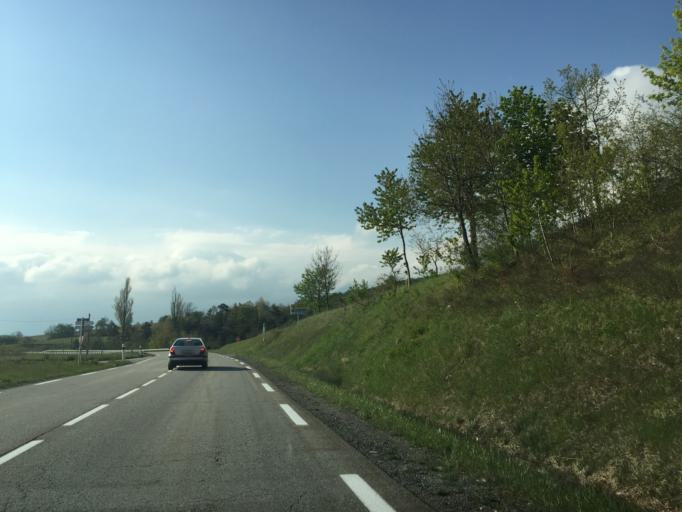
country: FR
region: Rhone-Alpes
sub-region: Departement de l'Isere
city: Mens
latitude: 44.8205
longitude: 5.6254
